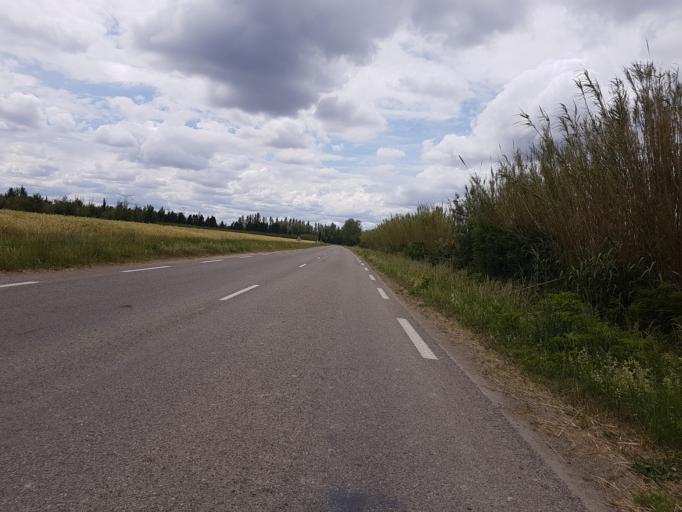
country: FR
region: Languedoc-Roussillon
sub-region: Departement du Gard
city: Vallabregues
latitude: 43.8819
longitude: 4.6330
